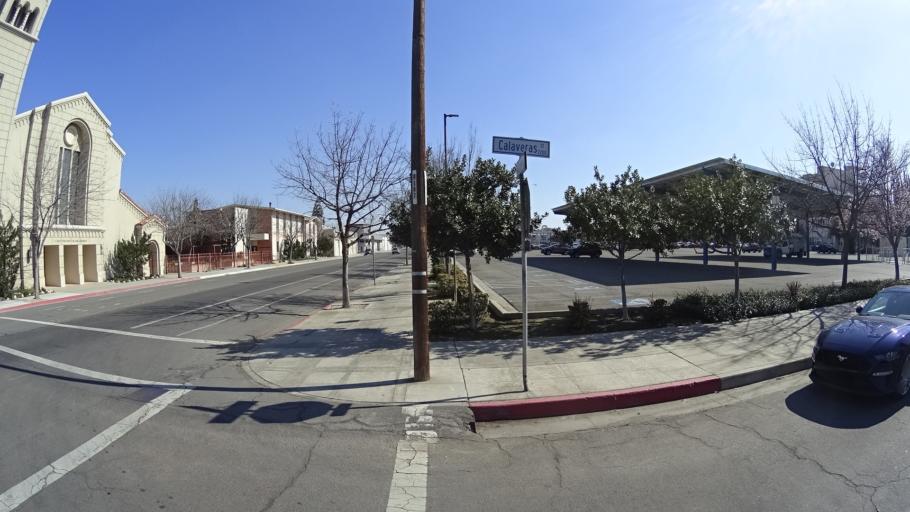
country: US
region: California
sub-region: Fresno County
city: Fresno
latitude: 36.7420
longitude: -119.7938
